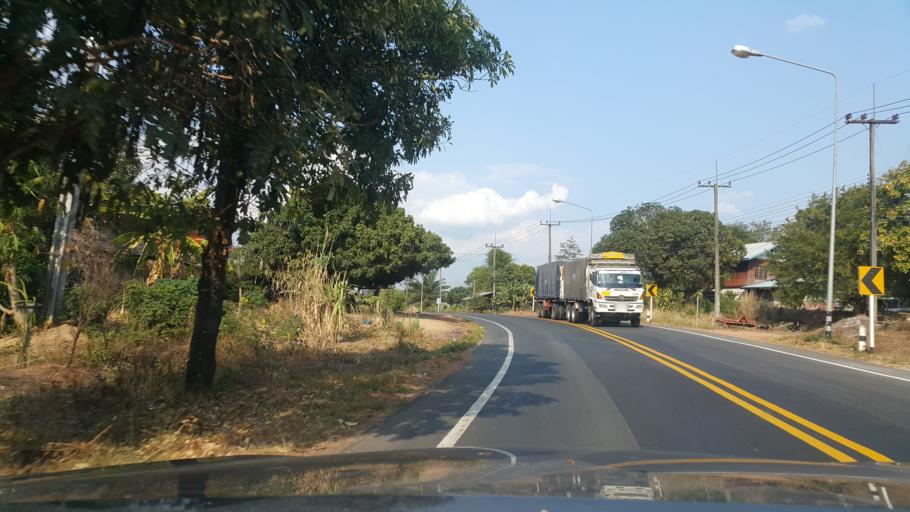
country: TH
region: Phitsanulok
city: Nakhon Thai
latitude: 17.1603
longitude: 100.9664
